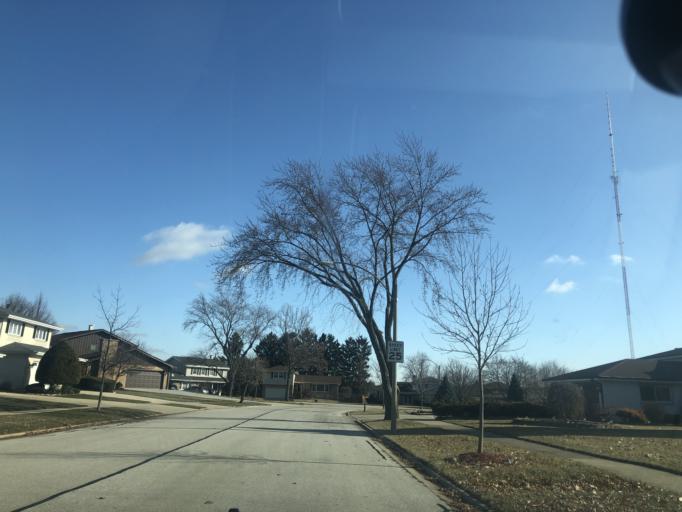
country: US
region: Illinois
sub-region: DuPage County
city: Addison
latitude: 41.9288
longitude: -88.0101
